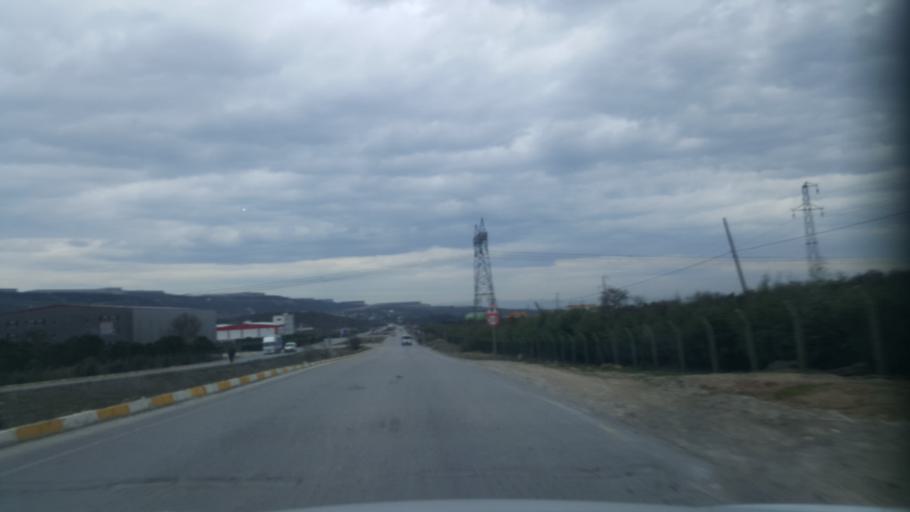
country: TR
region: Kocaeli
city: Tavsanli
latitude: 40.8633
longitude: 29.5591
